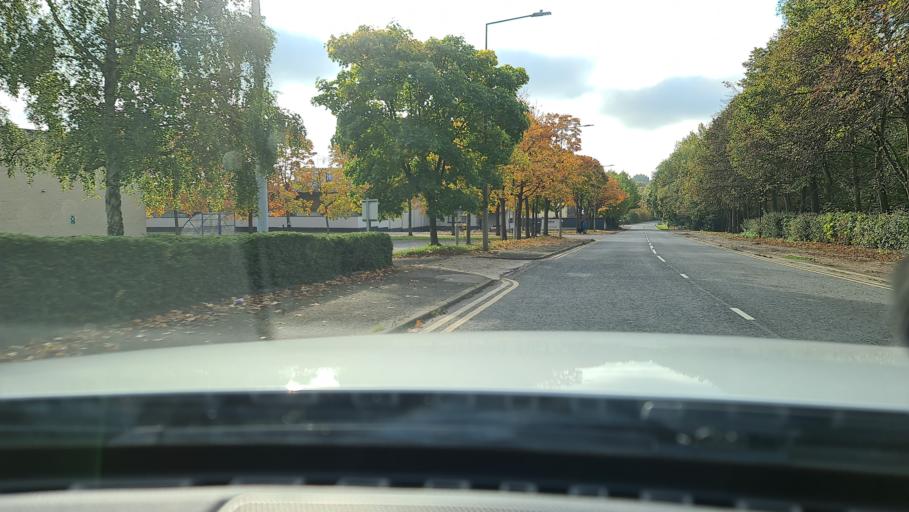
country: GB
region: England
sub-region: Buckinghamshire
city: Bletchley
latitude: 52.0088
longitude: -0.7205
